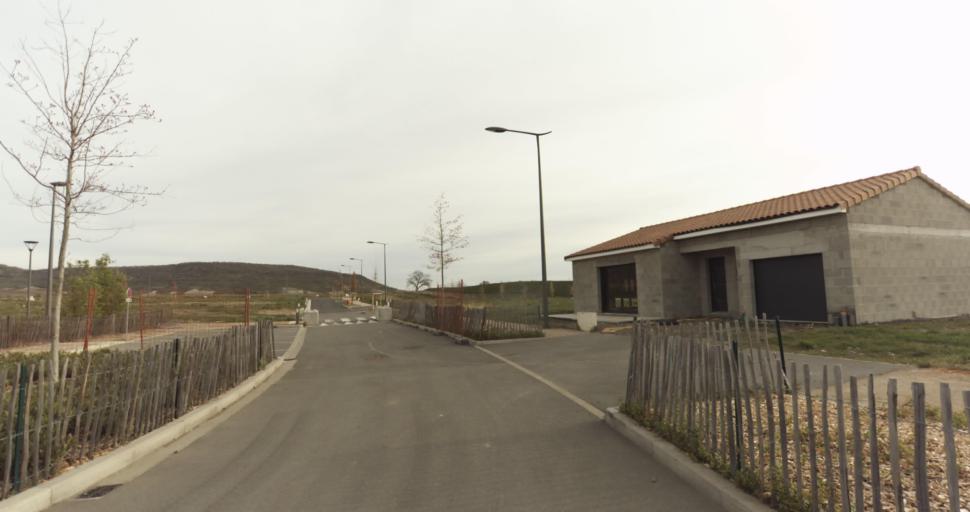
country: FR
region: Auvergne
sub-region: Departement du Puy-de-Dome
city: Cebazat
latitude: 45.8403
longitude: 3.1097
